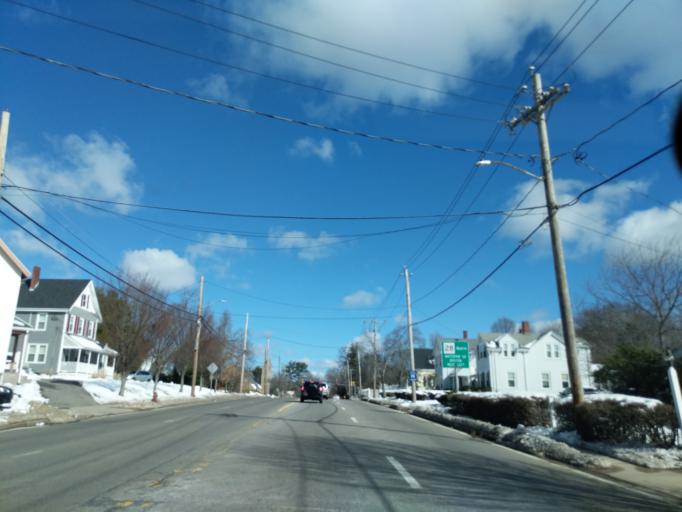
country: US
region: Massachusetts
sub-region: Norfolk County
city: Milton
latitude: 42.2469
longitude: -71.0692
